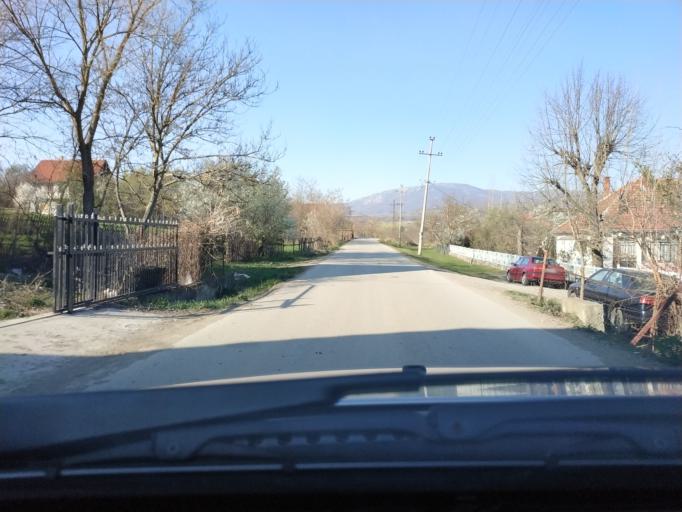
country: RS
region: Central Serbia
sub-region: Nisavski Okrug
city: Aleksinac
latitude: 43.5135
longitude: 21.7989
